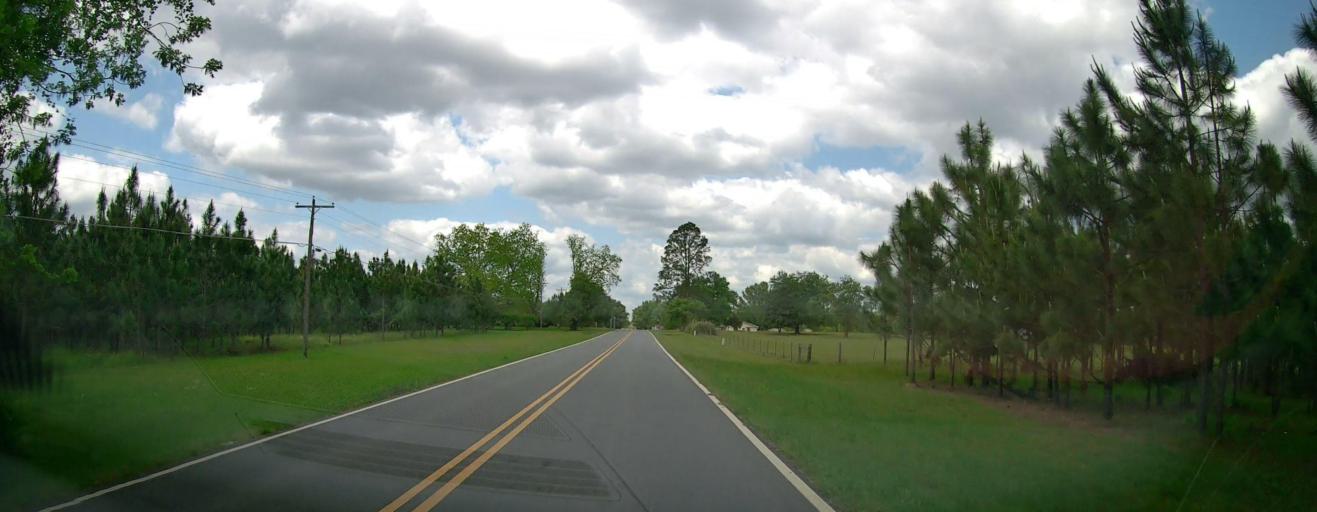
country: US
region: Georgia
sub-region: Laurens County
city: Dublin
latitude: 32.6060
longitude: -82.9614
